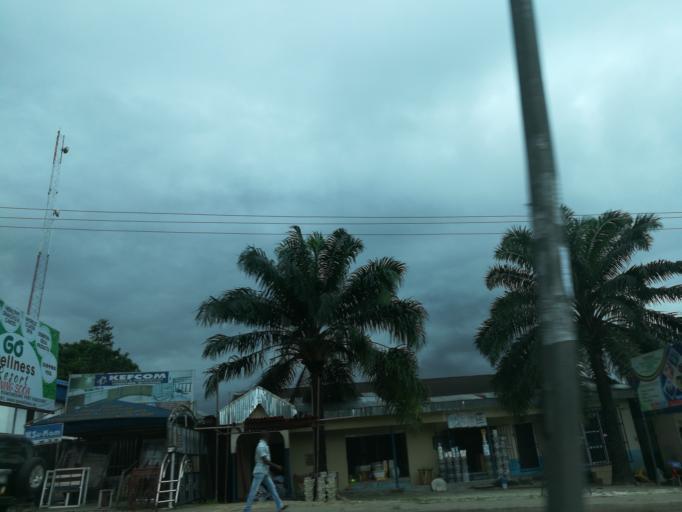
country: NG
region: Rivers
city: Port Harcourt
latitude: 4.8384
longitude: 7.0378
